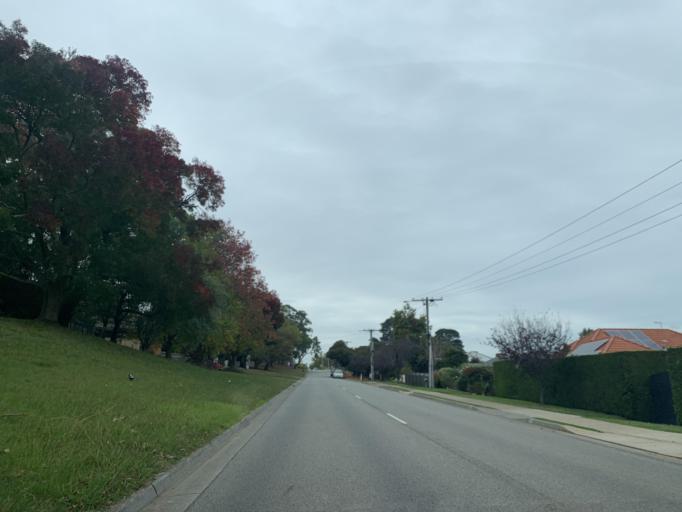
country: AU
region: Victoria
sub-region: Casey
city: Berwick
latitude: -38.0286
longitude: 145.3531
